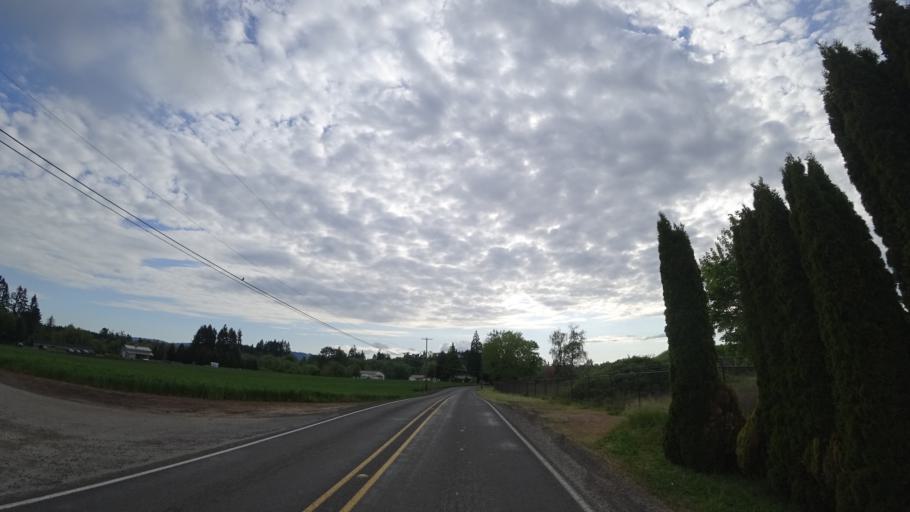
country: US
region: Oregon
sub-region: Washington County
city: Hillsboro
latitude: 45.4873
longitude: -122.9758
